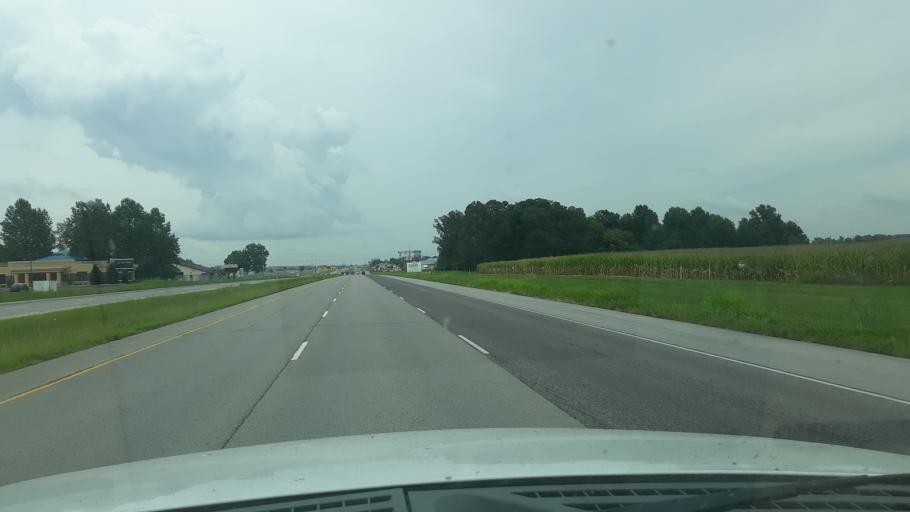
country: US
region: Illinois
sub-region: Williamson County
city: Energy
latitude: 37.7450
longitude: -89.0285
